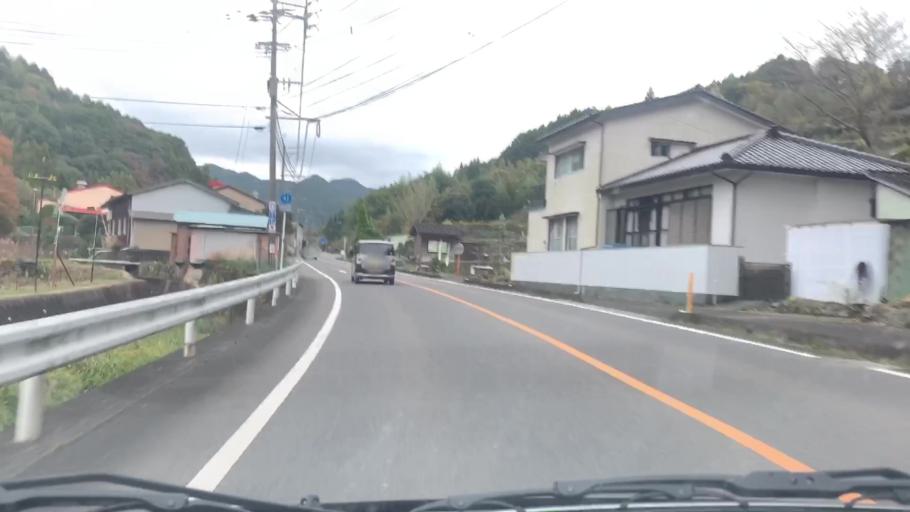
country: JP
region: Saga Prefecture
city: Ureshinomachi-shimojuku
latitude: 33.0898
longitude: 130.0086
